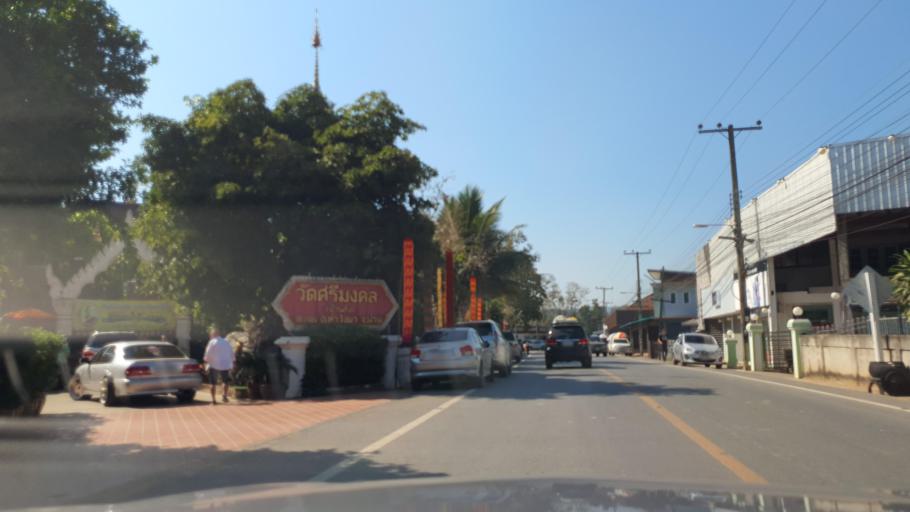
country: TH
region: Nan
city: Tha Wang Pha
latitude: 19.0830
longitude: 100.8883
